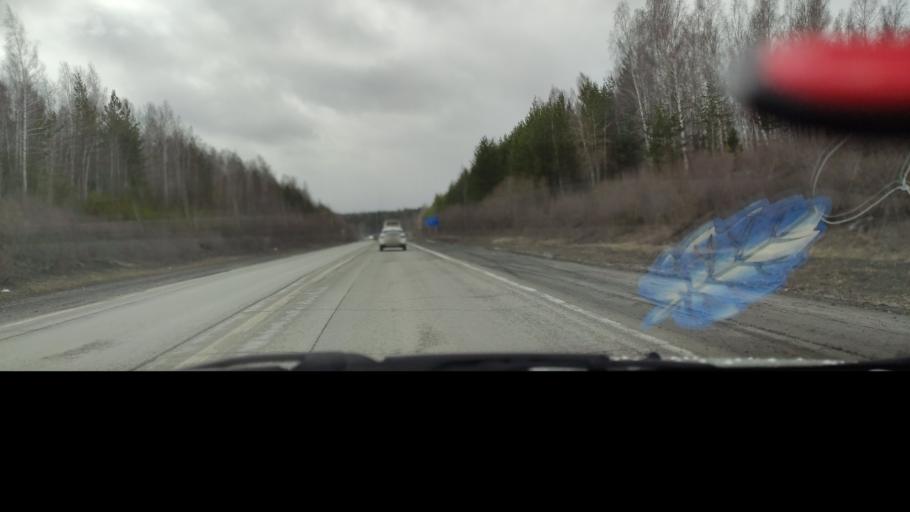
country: RU
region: Sverdlovsk
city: Talitsa
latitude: 56.8509
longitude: 60.0593
